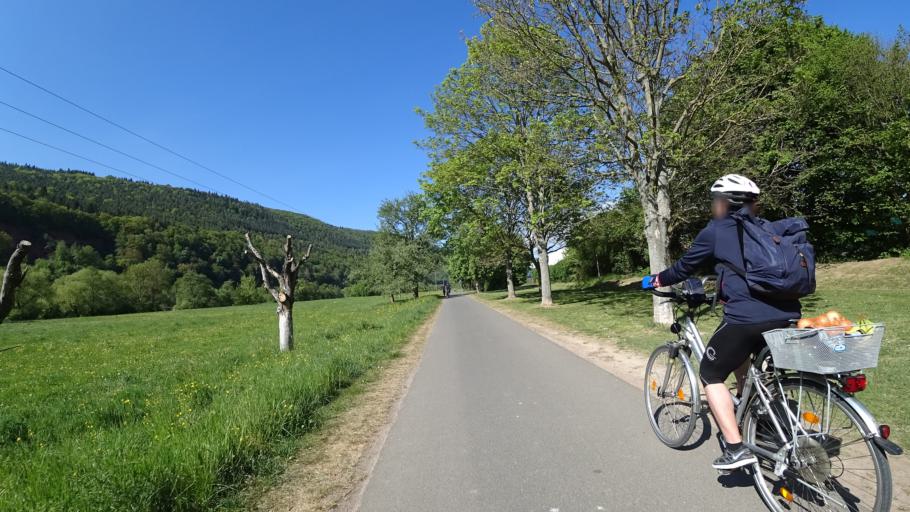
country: DE
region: Bavaria
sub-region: Regierungsbezirk Unterfranken
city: Burgstadt
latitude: 49.7264
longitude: 9.2690
